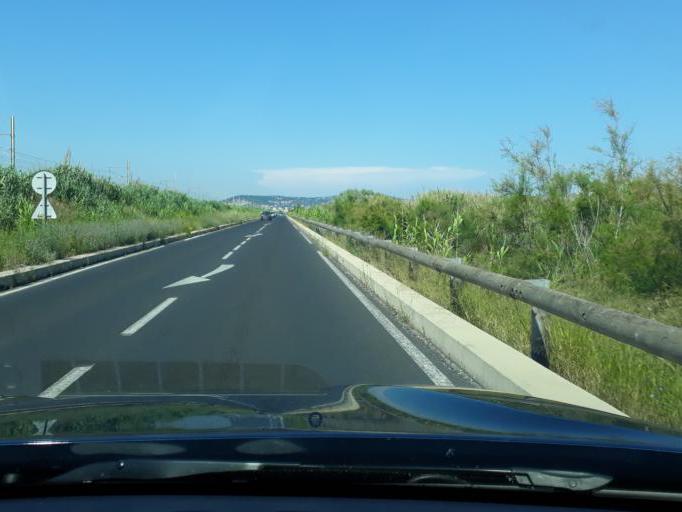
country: FR
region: Languedoc-Roussillon
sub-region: Departement de l'Herault
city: Meze
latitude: 43.3691
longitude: 3.6180
